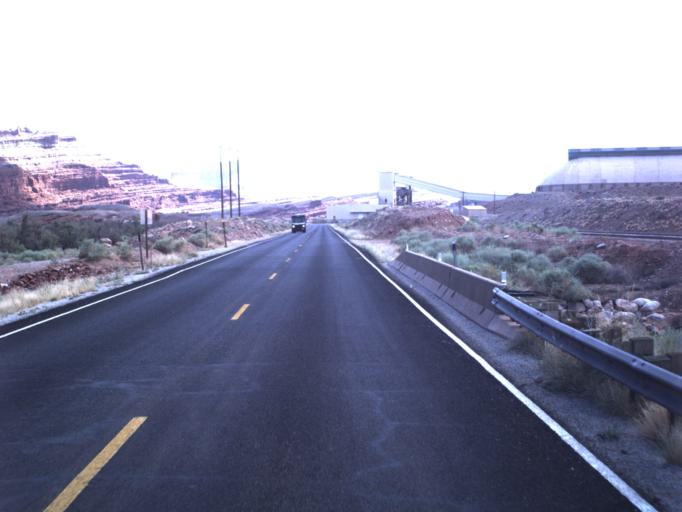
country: US
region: Utah
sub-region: Grand County
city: Moab
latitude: 38.5276
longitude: -109.6555
